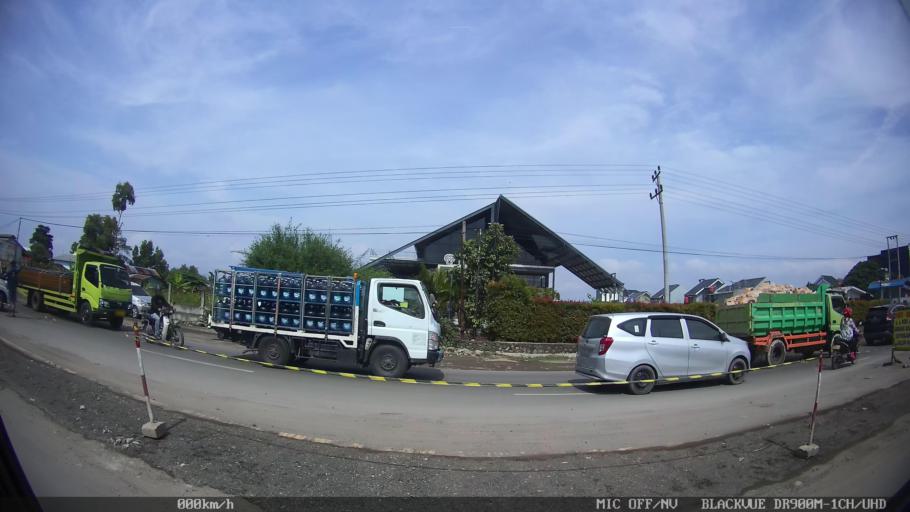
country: ID
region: Lampung
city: Kedaton
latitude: -5.3939
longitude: 105.2891
